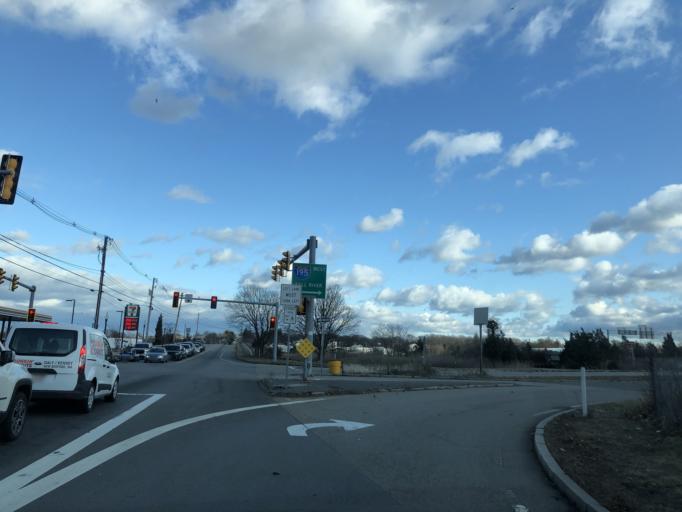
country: US
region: Massachusetts
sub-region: Bristol County
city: New Bedford
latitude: 41.6561
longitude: -70.9201
